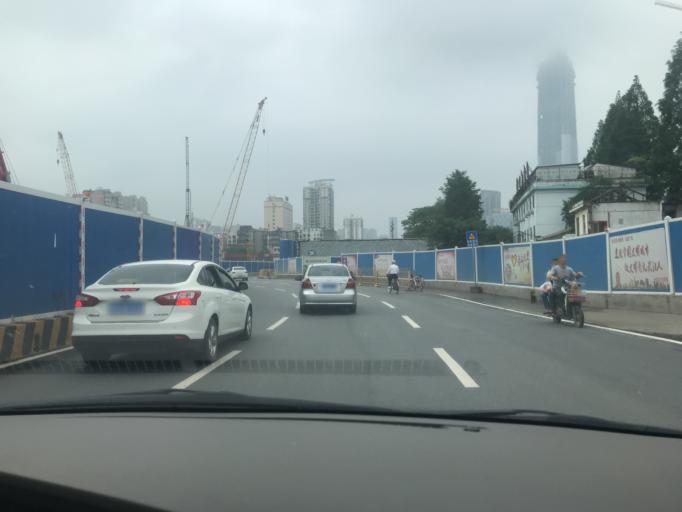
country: CN
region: Hubei
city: Jiang'an
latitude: 30.5931
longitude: 114.3275
